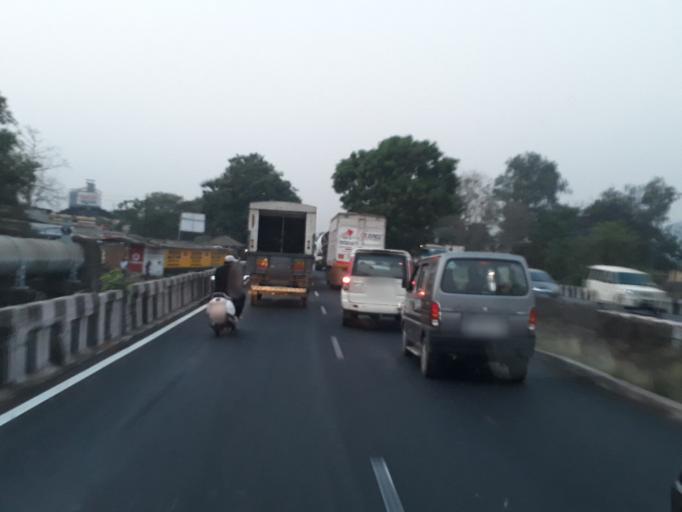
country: IN
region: Maharashtra
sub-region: Raigarh
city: Kalundri
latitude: 18.9328
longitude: 73.1916
